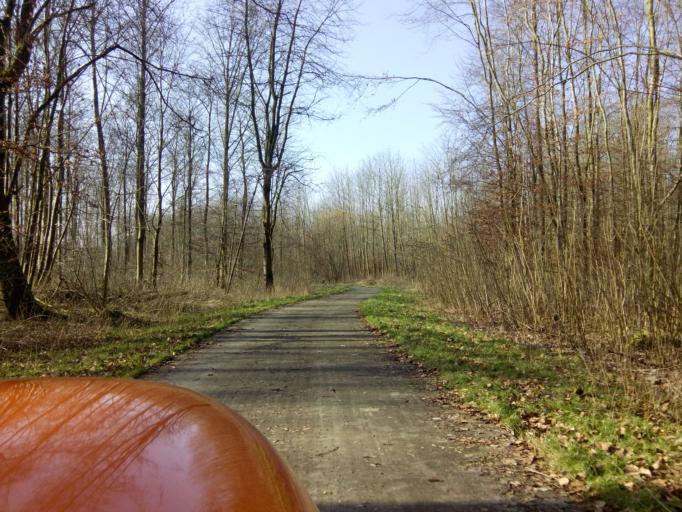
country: NL
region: Flevoland
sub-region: Gemeente Zeewolde
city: Zeewolde
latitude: 52.2926
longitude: 5.5021
